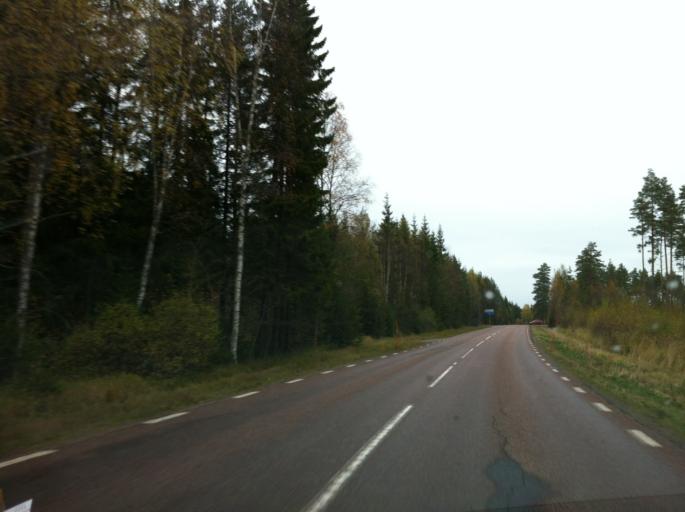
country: SE
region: Dalarna
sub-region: Ludvika Kommun
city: Grangesberg
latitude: 60.1265
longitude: 15.0065
